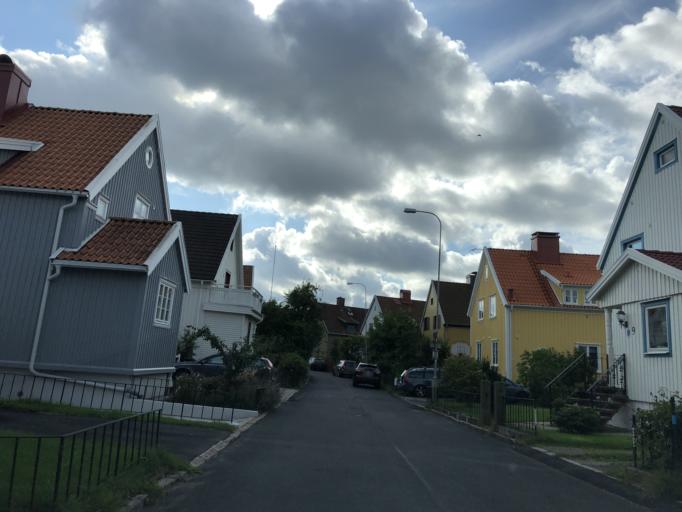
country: SE
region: Vaestra Goetaland
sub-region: Goteborg
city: Goeteborg
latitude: 57.7151
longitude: 12.0200
